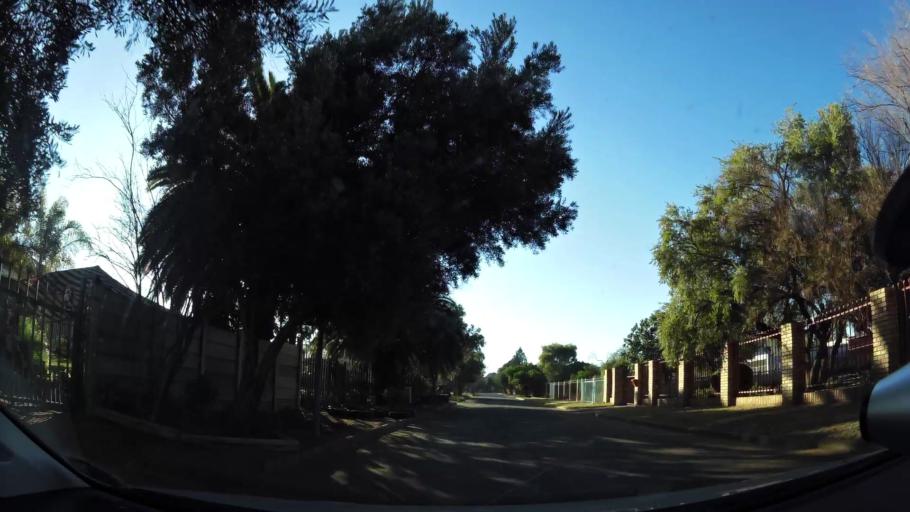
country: ZA
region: Northern Cape
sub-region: Frances Baard District Municipality
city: Kimberley
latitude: -28.7417
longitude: 24.7327
